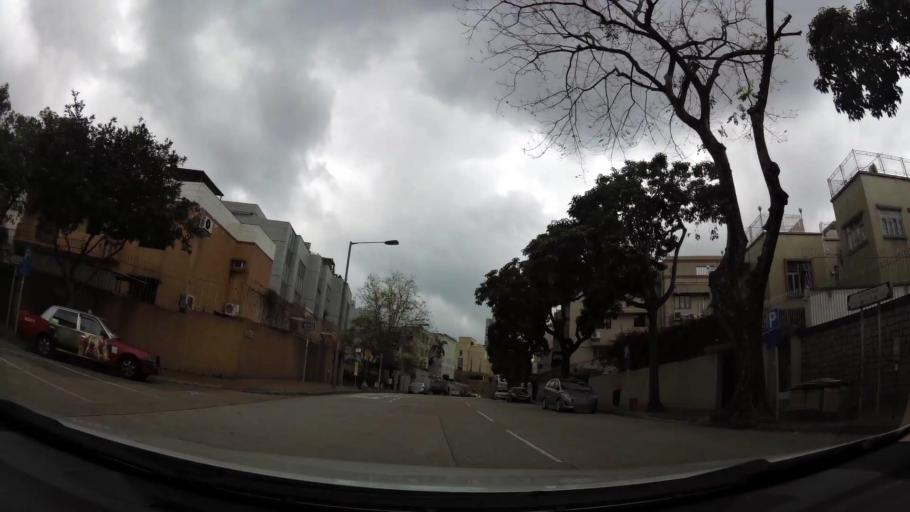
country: HK
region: Kowloon City
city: Kowloon
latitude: 22.3316
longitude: 114.1819
